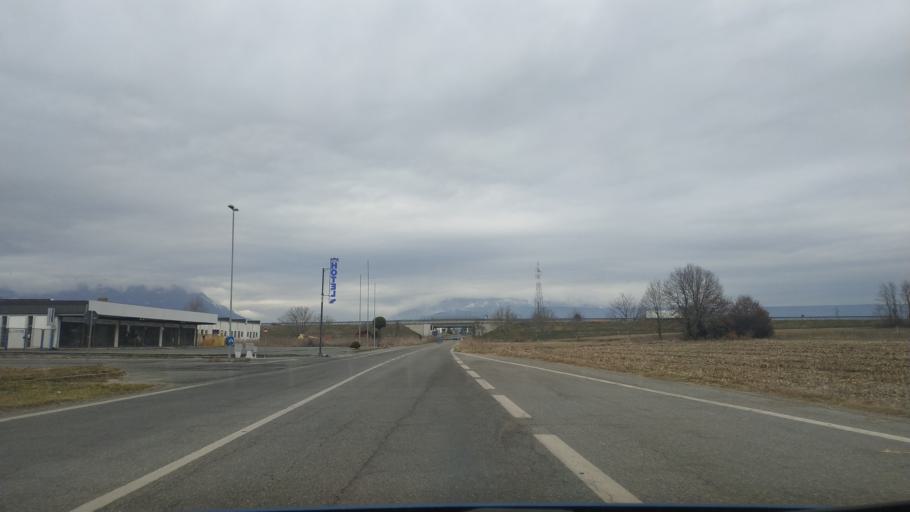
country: IT
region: Piedmont
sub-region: Provincia di Torino
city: Romano Canavese
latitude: 45.4190
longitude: 7.8832
